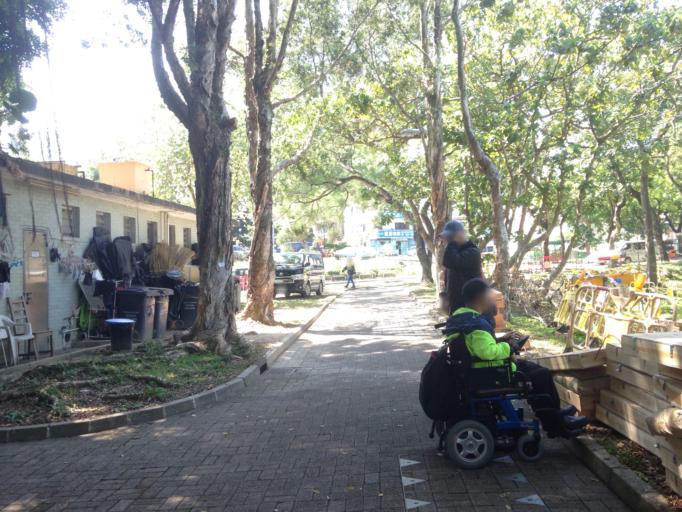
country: HK
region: Sai Kung
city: Sai Kung
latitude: 22.4309
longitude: 114.2552
